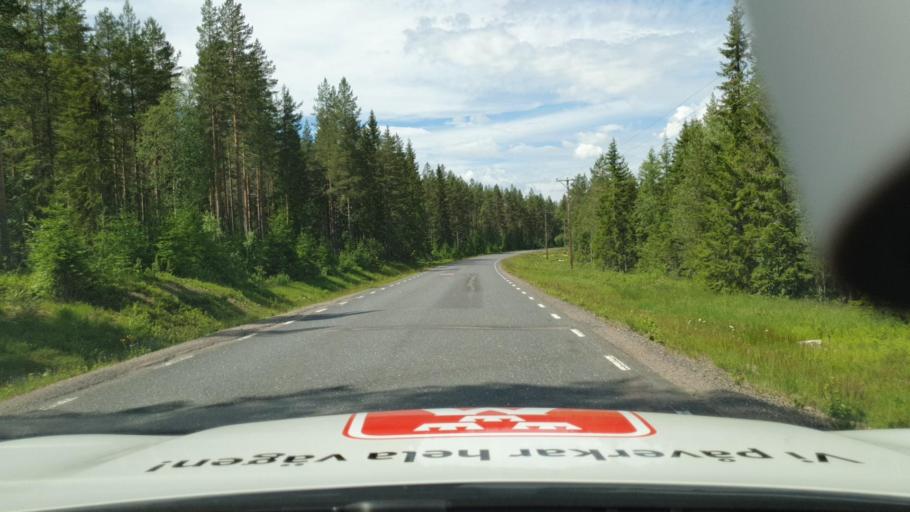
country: SE
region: Vaermland
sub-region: Torsby Kommun
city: Torsby
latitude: 60.5568
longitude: 12.7666
